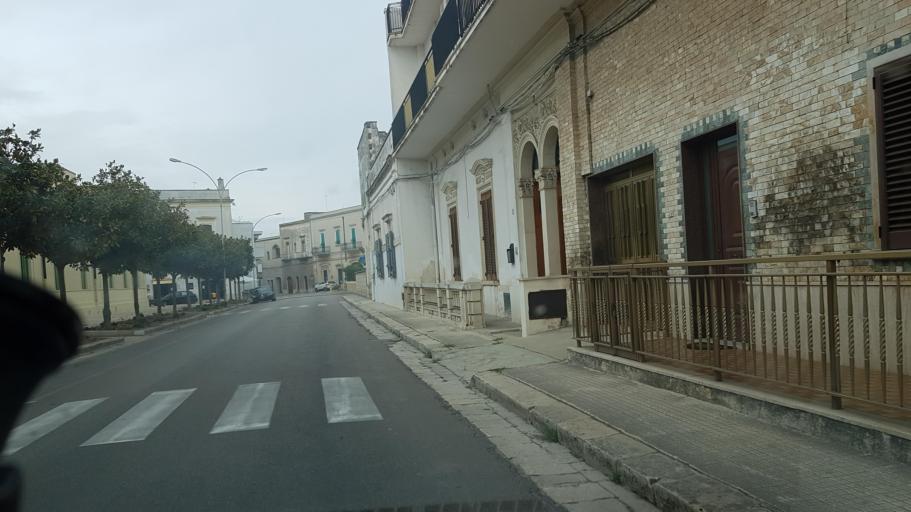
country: IT
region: Apulia
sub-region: Provincia di Lecce
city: Leverano
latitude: 40.2895
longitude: 18.0031
